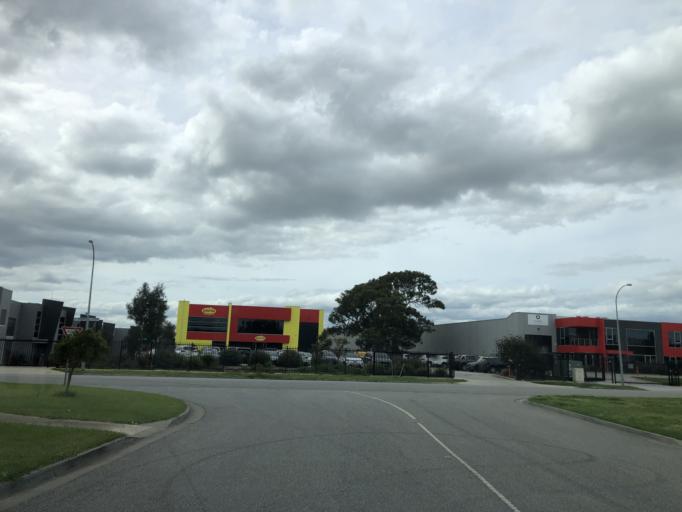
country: AU
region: Victoria
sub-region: Frankston
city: Carrum Downs
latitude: -38.0909
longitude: 145.1680
